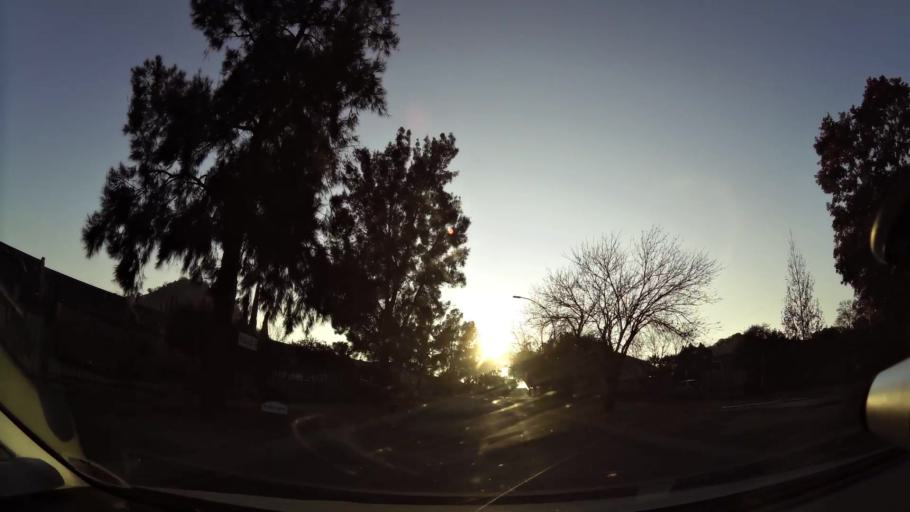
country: ZA
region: Orange Free State
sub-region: Mangaung Metropolitan Municipality
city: Bloemfontein
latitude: -29.0962
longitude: 26.1557
